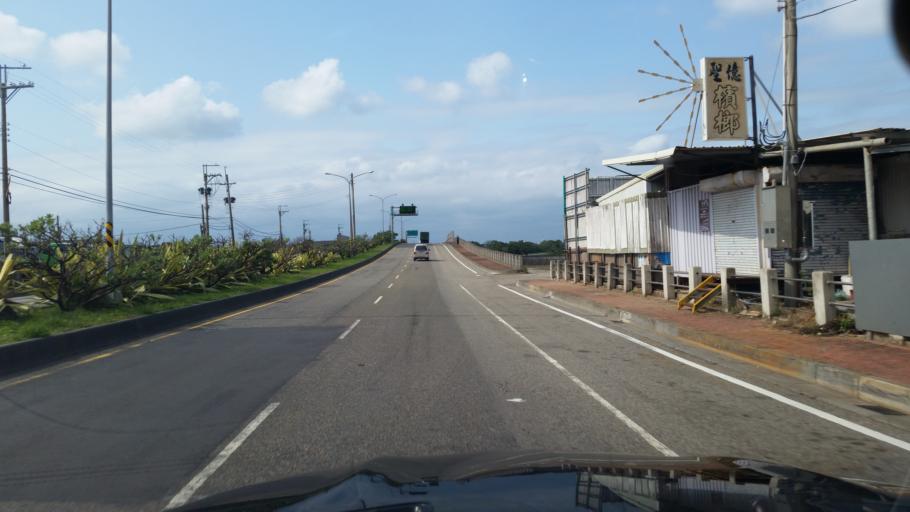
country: TW
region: Taiwan
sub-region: Miaoli
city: Miaoli
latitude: 24.6733
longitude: 120.8522
